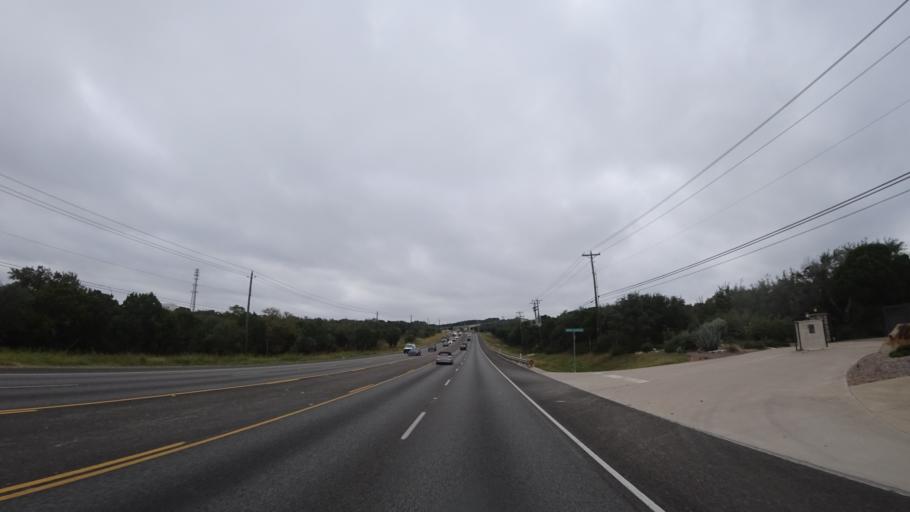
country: US
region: Texas
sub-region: Travis County
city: Bee Cave
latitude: 30.2850
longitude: -97.9166
